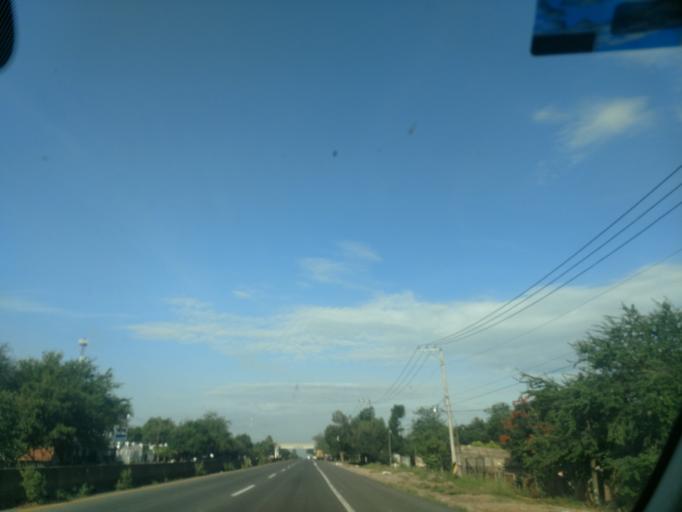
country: MX
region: Jalisco
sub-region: Ameca
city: Los Pocitos
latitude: 20.5373
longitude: -103.9346
